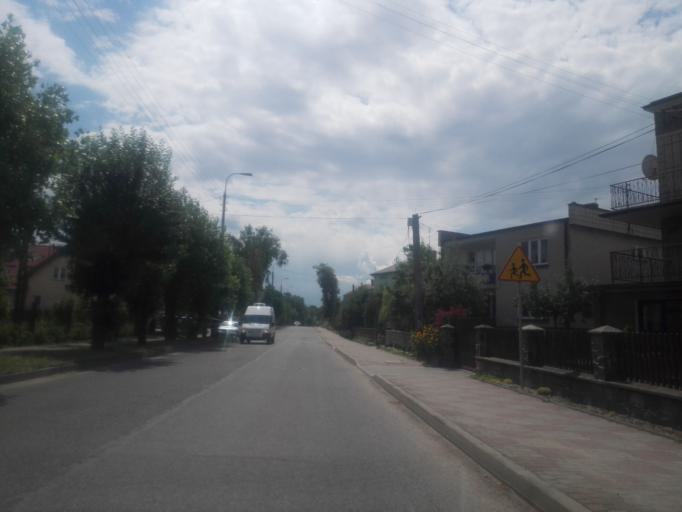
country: PL
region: Podlasie
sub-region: Powiat sejnenski
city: Sejny
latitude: 54.1132
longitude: 23.3520
